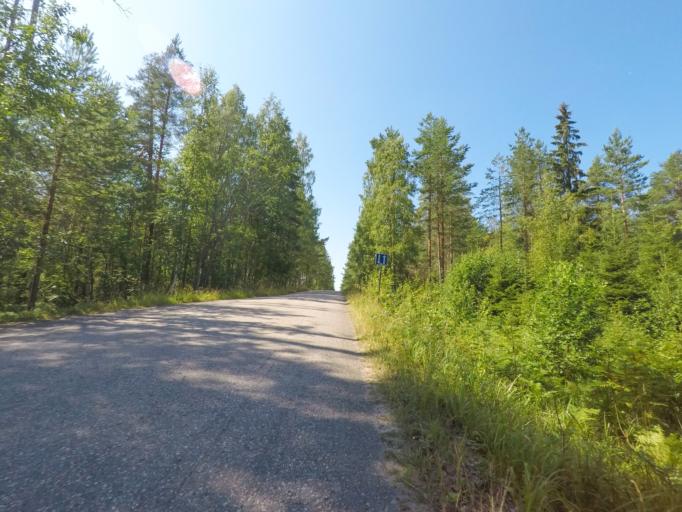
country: FI
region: Southern Savonia
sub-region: Mikkeli
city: Puumala
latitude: 61.4064
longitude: 28.0596
